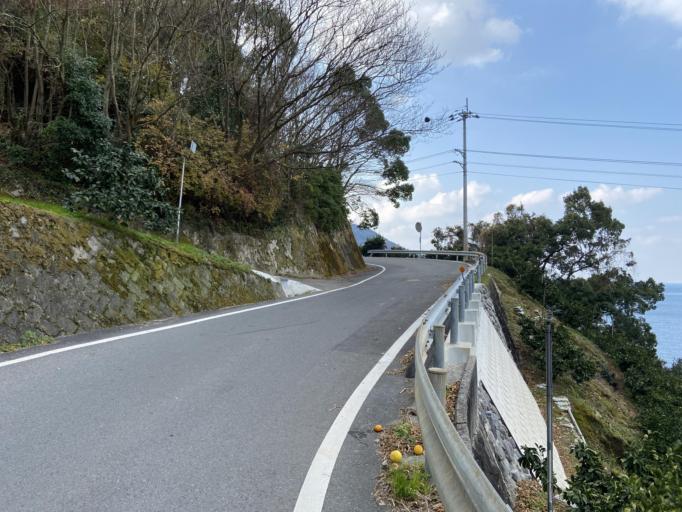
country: JP
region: Ehime
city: Uwajima
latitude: 33.2595
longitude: 132.5420
